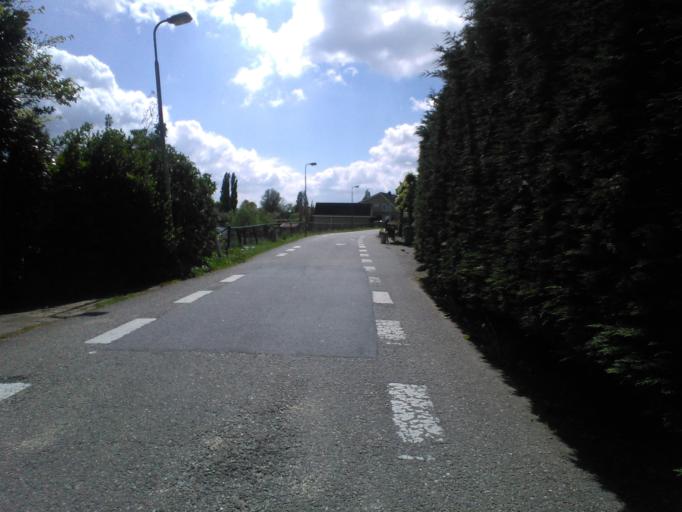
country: NL
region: South Holland
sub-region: Gemeente Hendrik-Ido-Ambacht
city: Hendrik-Ido-Ambacht
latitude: 51.8533
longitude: 4.6223
